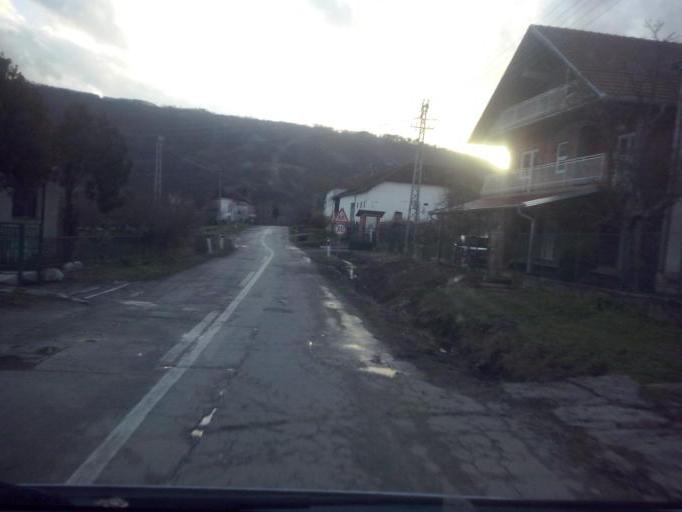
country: RS
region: Central Serbia
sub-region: Pirotski Okrug
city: Bela Palanka
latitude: 43.0367
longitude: 22.4078
